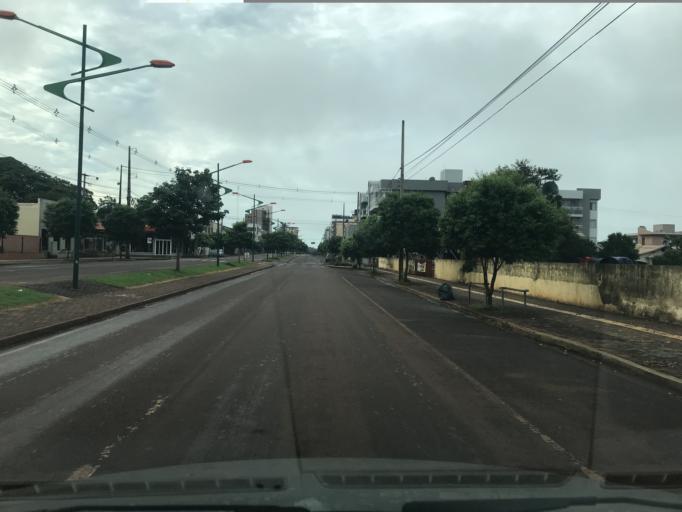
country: BR
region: Parana
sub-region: Palotina
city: Palotina
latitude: -24.2891
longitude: -53.8380
